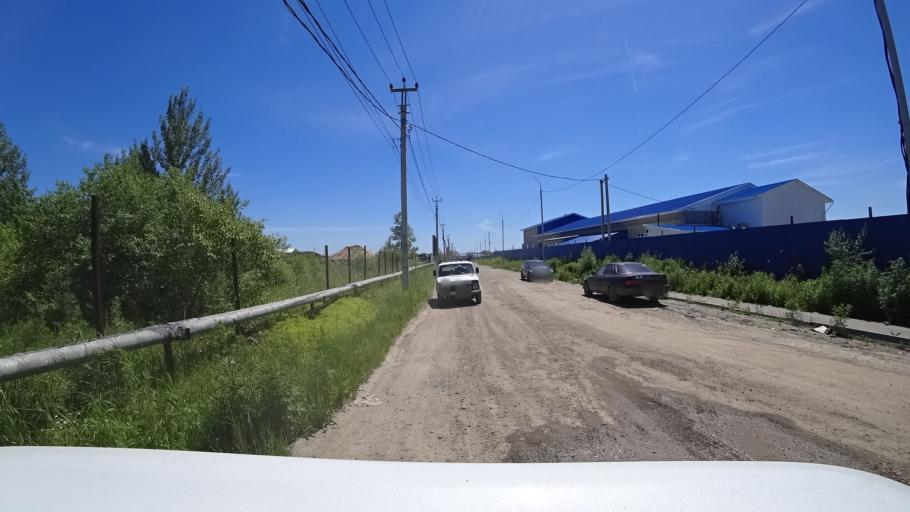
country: RU
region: Khabarovsk Krai
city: Topolevo
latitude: 48.5047
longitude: 135.1810
